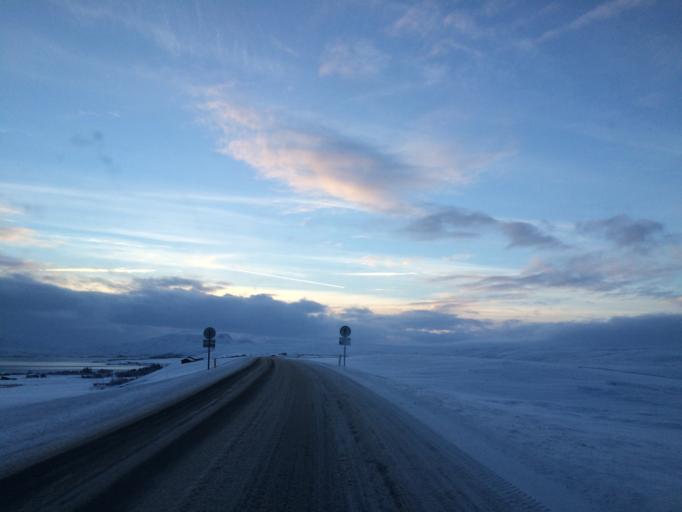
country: IS
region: South
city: Hveragerdi
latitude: 64.2378
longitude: -21.1904
